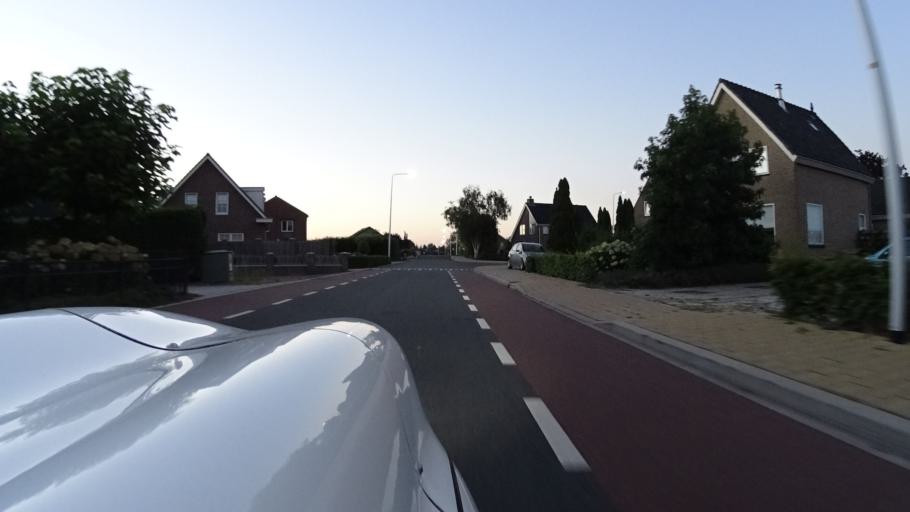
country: NL
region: South Holland
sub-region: Gemeente Kaag en Braassem
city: Oude Wetering
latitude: 52.1943
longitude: 4.6201
